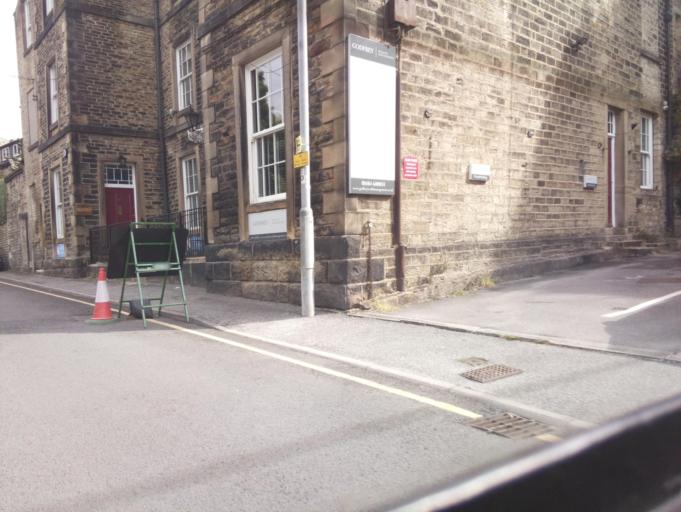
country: GB
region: England
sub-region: Kirklees
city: Holmfirth
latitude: 53.5716
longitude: -1.7842
